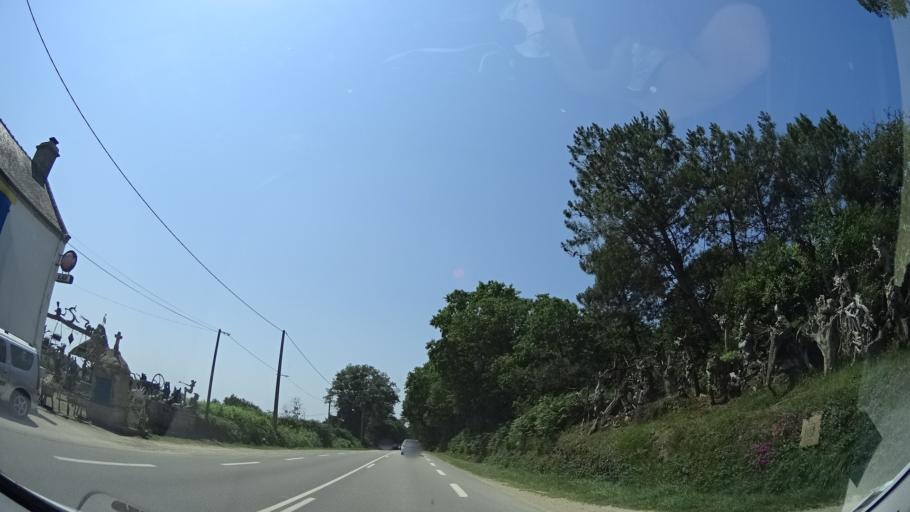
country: FR
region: Brittany
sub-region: Departement du Morbihan
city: Ploemel
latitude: 47.6460
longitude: -3.0388
